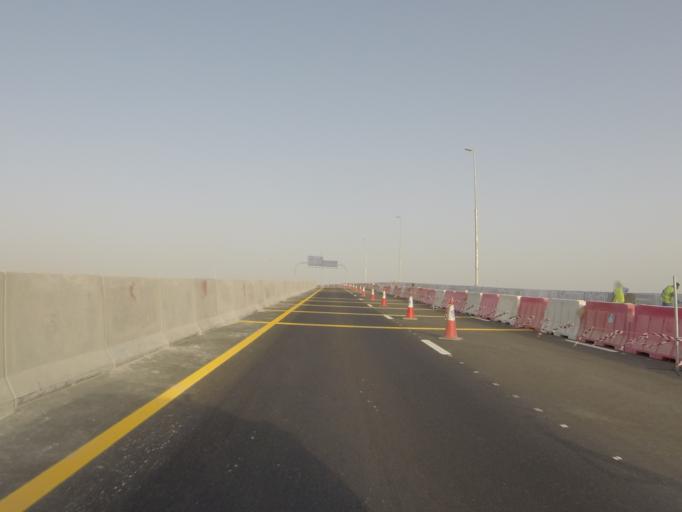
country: AE
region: Dubai
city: Dubai
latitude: 24.9209
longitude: 54.9905
